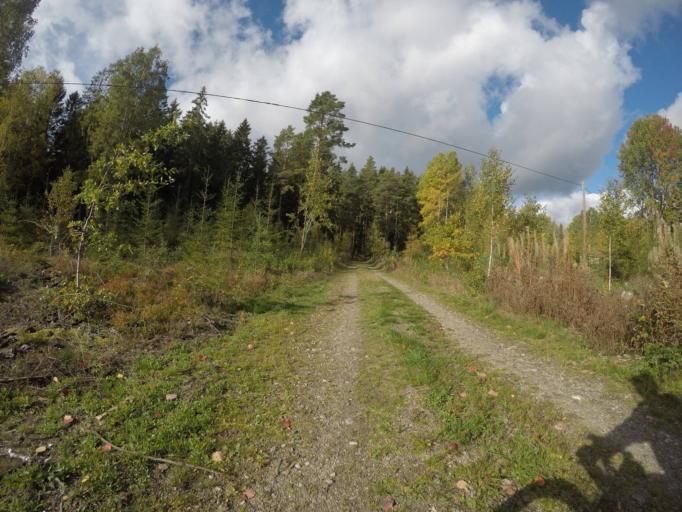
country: SE
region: Vaestmanland
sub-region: Kungsors Kommun
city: Kungsoer
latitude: 59.2866
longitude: 16.1157
